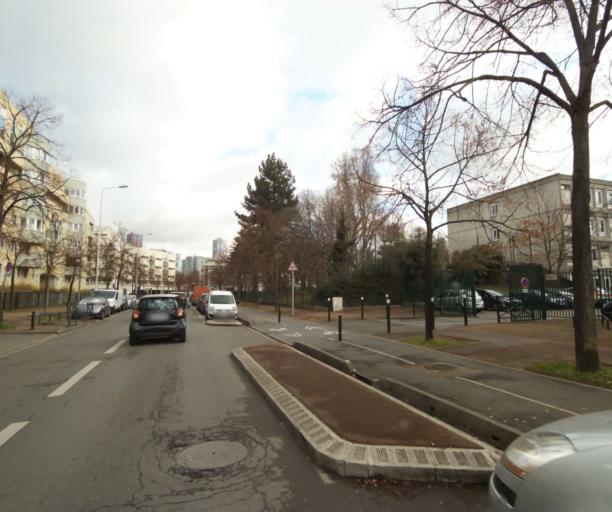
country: FR
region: Ile-de-France
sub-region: Departement des Hauts-de-Seine
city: Nanterre
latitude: 48.8903
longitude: 2.2175
